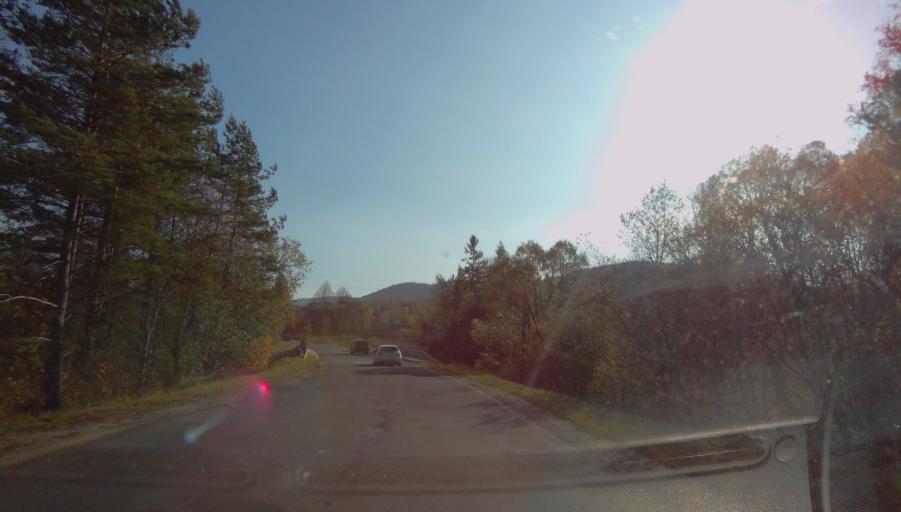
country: PL
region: Subcarpathian Voivodeship
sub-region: Powiat leski
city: Cisna
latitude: 49.2229
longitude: 22.1814
